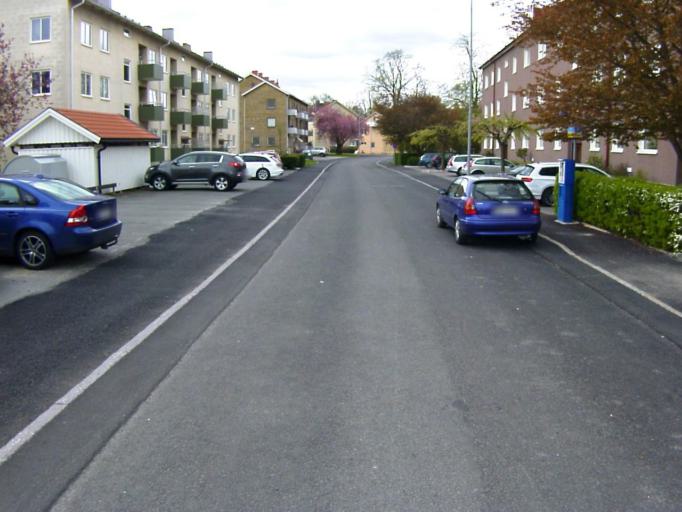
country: SE
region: Skane
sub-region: Kristianstads Kommun
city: Kristianstad
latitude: 56.0349
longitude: 14.1674
